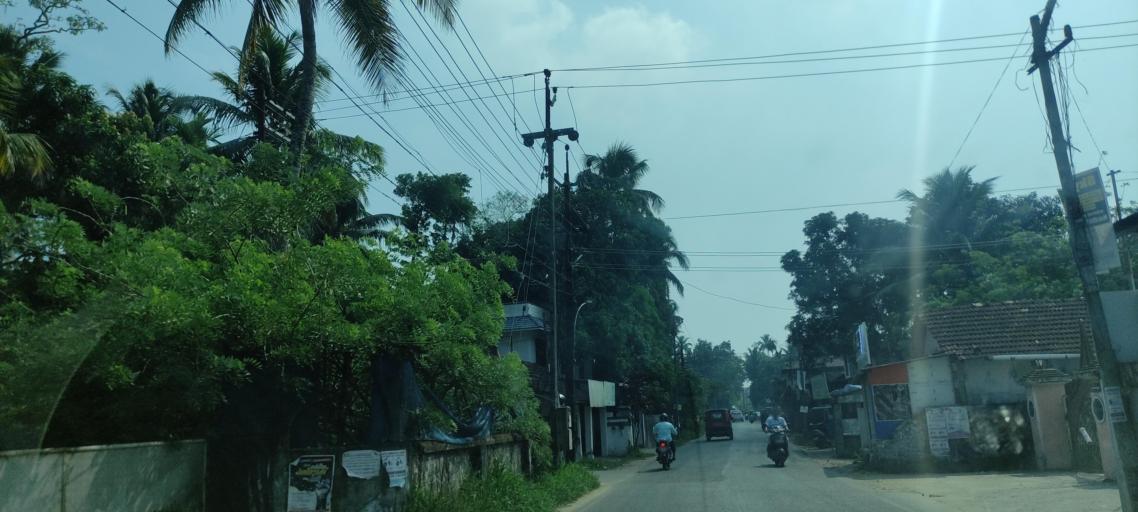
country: IN
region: Kerala
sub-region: Alappuzha
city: Kutiatodu
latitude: 9.8220
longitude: 76.3027
